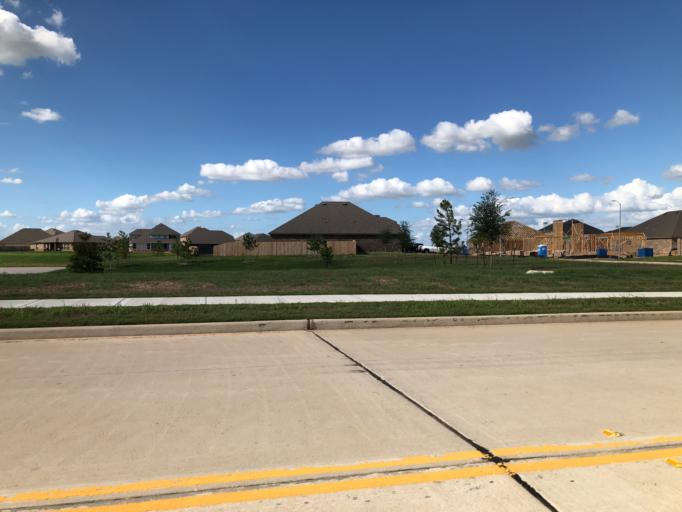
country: US
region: Texas
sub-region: Harris County
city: Katy
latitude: 29.8411
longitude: -95.7857
